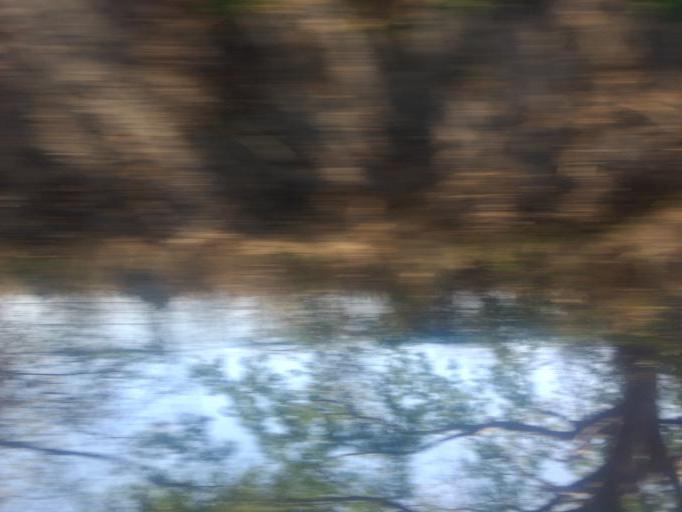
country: MX
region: Colima
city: Cuauhtemoc
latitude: 19.2966
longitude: -103.6426
